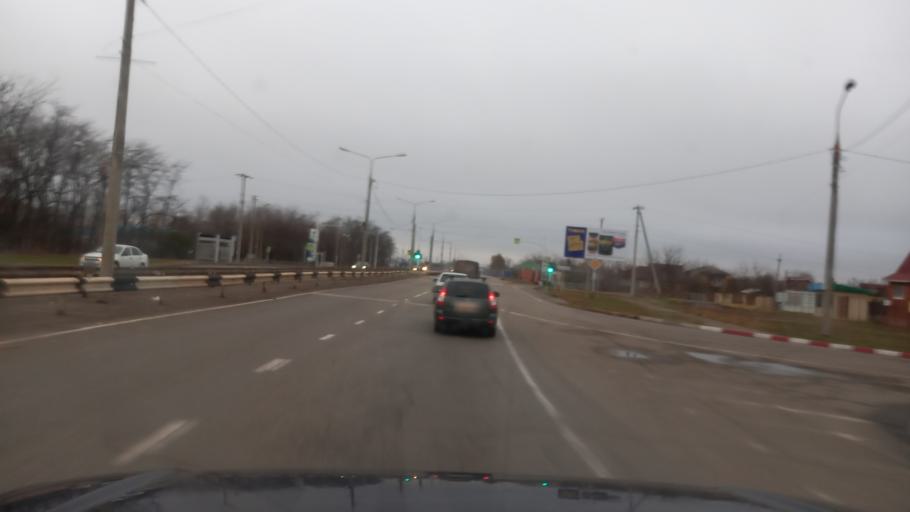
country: RU
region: Adygeya
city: Maykop
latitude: 44.6238
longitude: 40.0544
